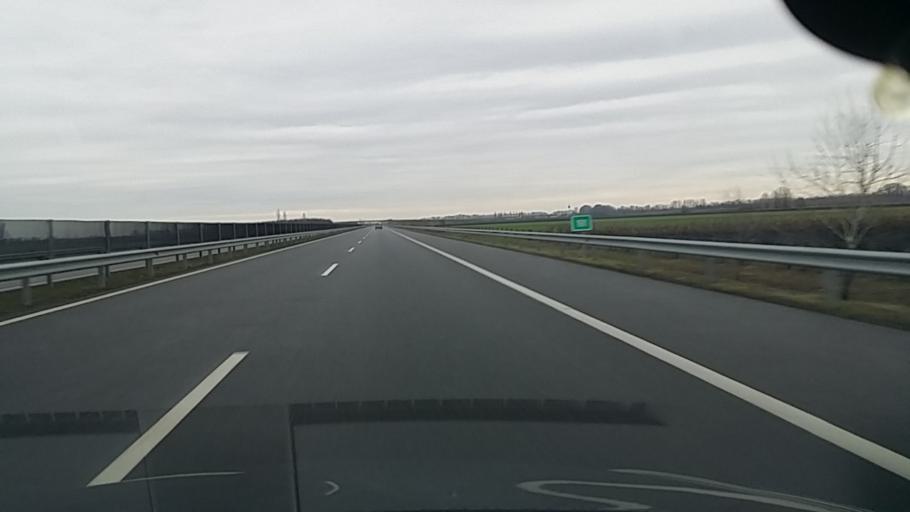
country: HU
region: Hajdu-Bihar
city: Gorbehaza
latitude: 47.8092
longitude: 21.3034
